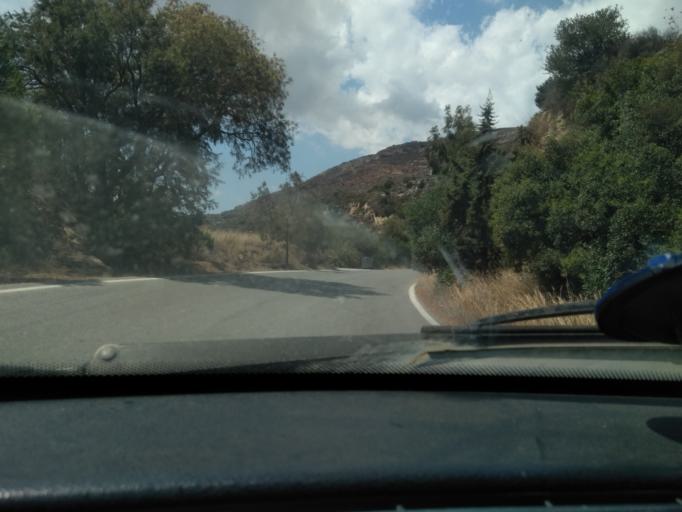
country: GR
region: Crete
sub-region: Nomos Lasithiou
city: Siteia
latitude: 35.1240
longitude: 26.0649
